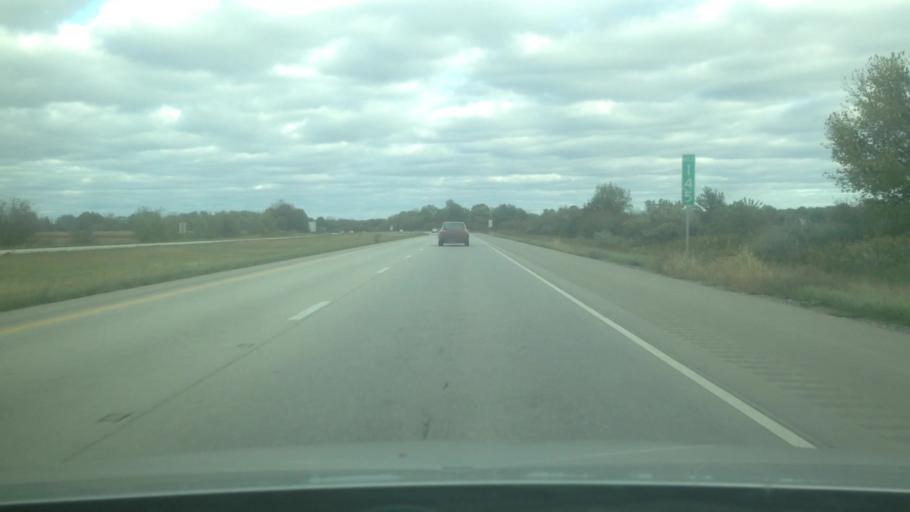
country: US
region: Illinois
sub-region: Macon County
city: Forsyth
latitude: 39.9105
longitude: -88.8828
